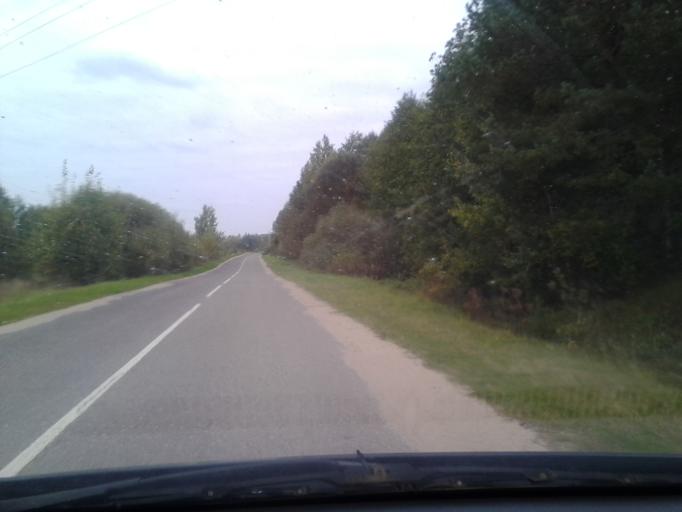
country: BY
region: Vitebsk
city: Pastavy
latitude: 55.0841
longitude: 26.8396
